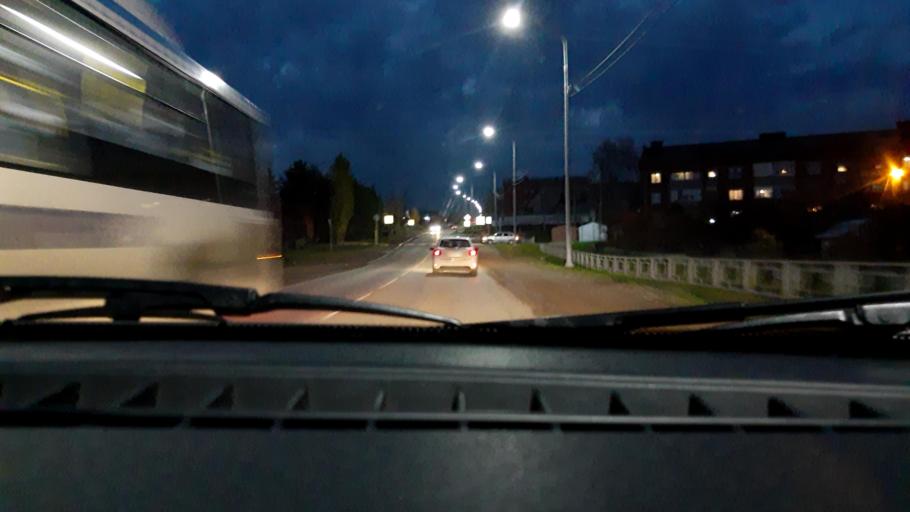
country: RU
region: Bashkortostan
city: Mikhaylovka
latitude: 54.8064
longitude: 55.8901
